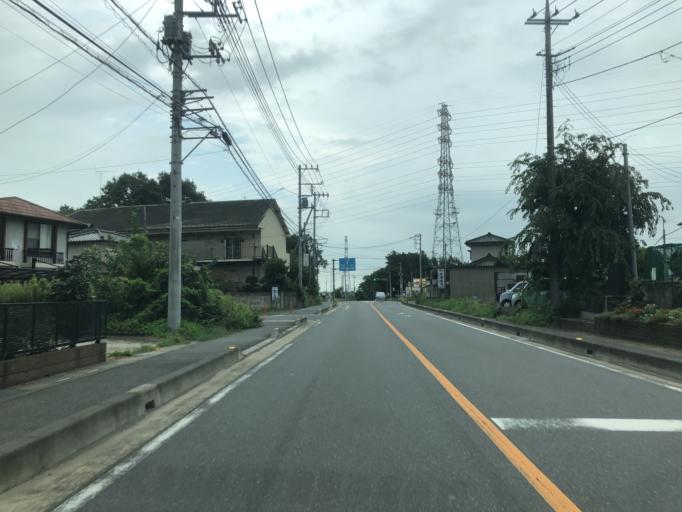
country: JP
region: Saitama
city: Sakado
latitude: 36.0016
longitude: 139.4061
